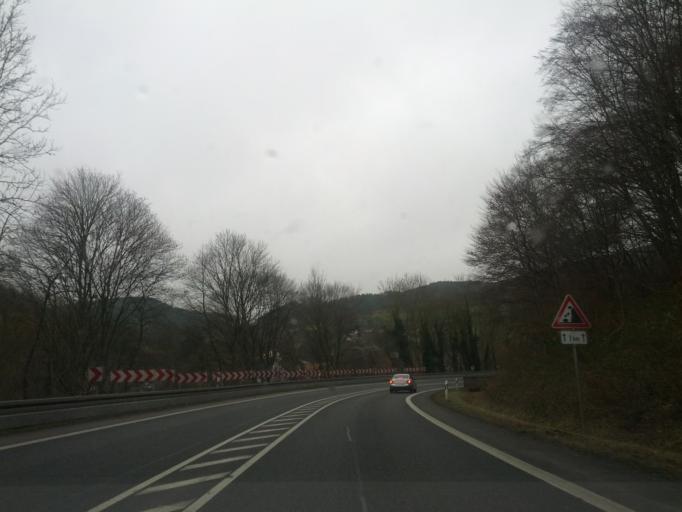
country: DE
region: Thuringia
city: Bornhagen
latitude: 51.3250
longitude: 9.9105
